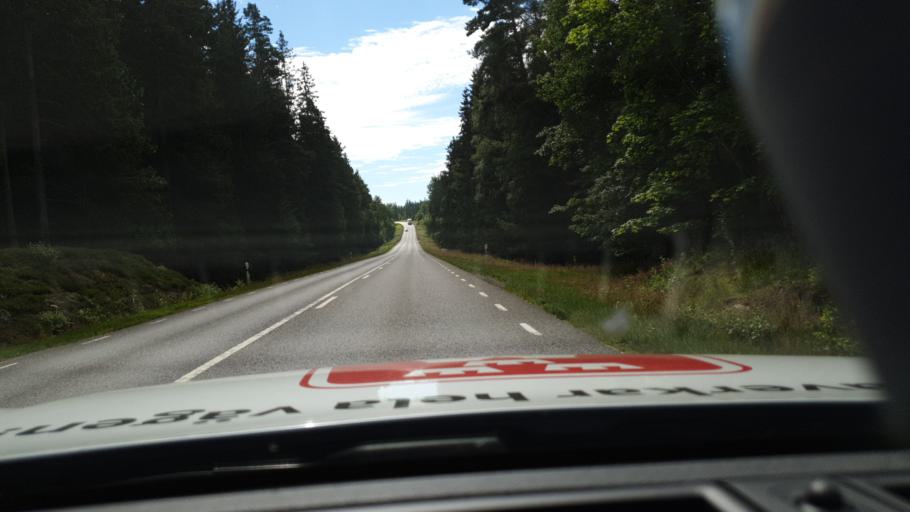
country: SE
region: Kronoberg
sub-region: Vaxjo Kommun
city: Lammhult
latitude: 57.2229
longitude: 14.5091
